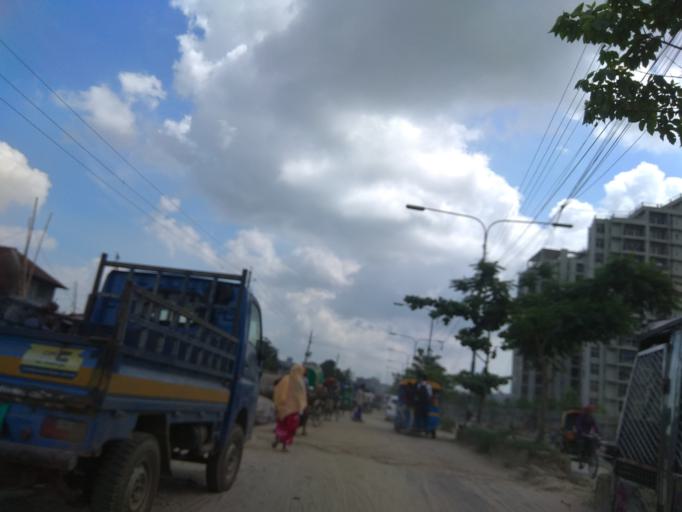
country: BD
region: Dhaka
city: Paltan
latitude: 23.8085
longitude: 90.3904
